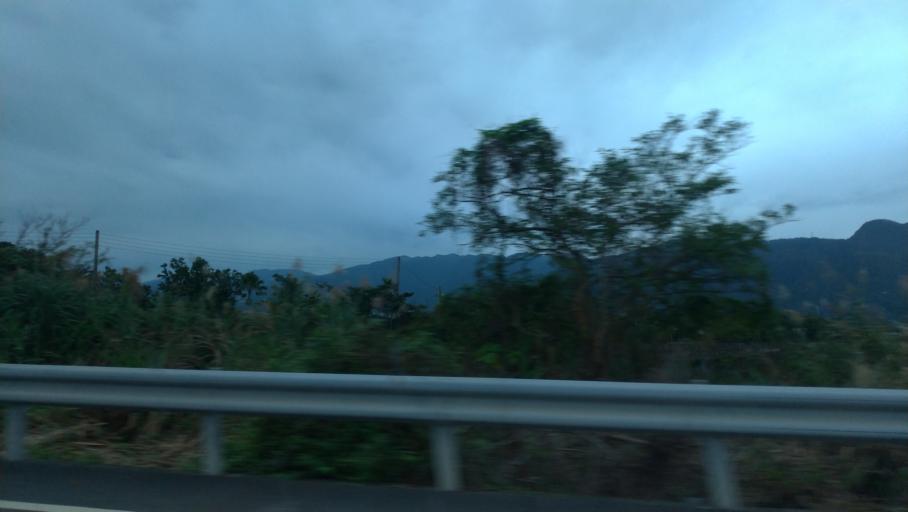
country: TW
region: Taiwan
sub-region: Yilan
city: Yilan
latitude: 24.8202
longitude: 121.7972
